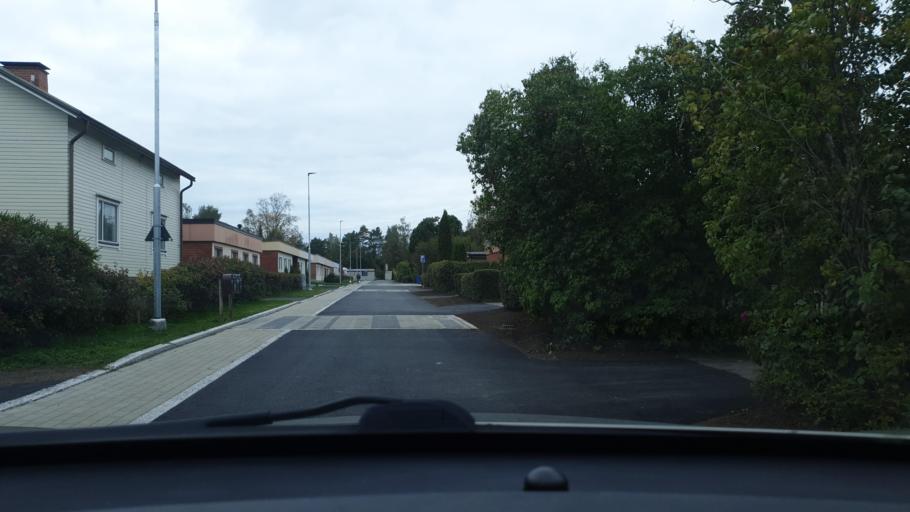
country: FI
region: Ostrobothnia
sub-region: Vaasa
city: Korsholm
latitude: 63.0955
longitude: 21.6723
